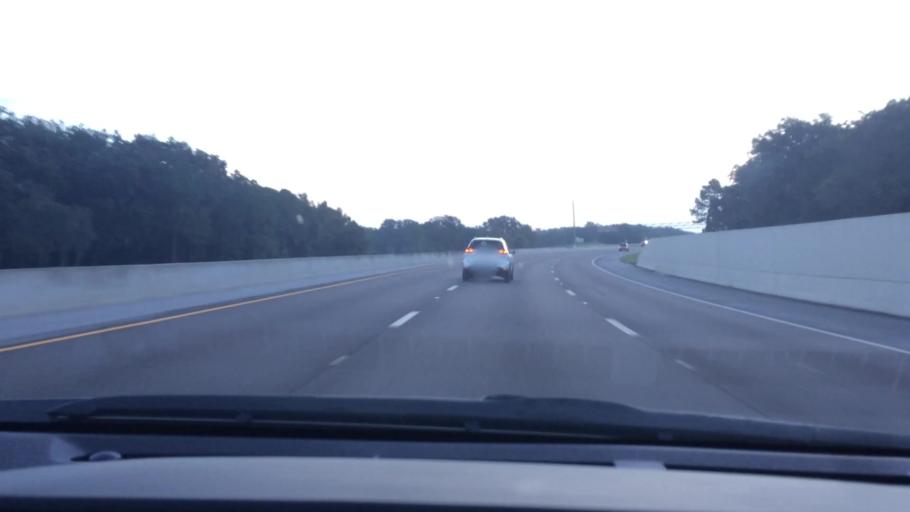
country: US
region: Florida
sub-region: Hillsborough County
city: Lake Magdalene
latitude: 28.0991
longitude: -82.4506
